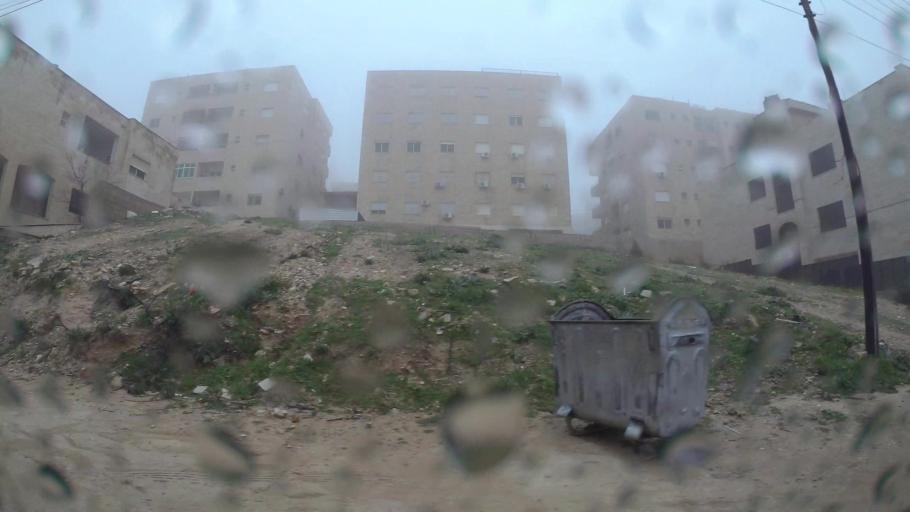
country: JO
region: Amman
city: Al Jubayhah
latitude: 32.0149
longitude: 35.8875
